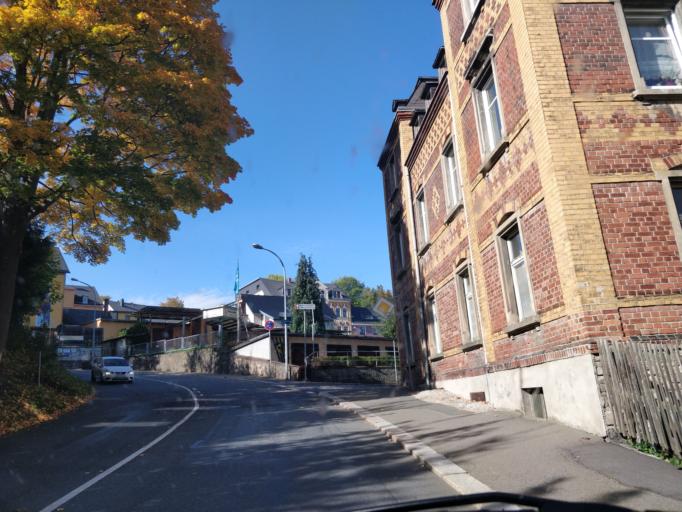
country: DE
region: Saxony
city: Schneeberg
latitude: 50.5987
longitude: 12.6429
